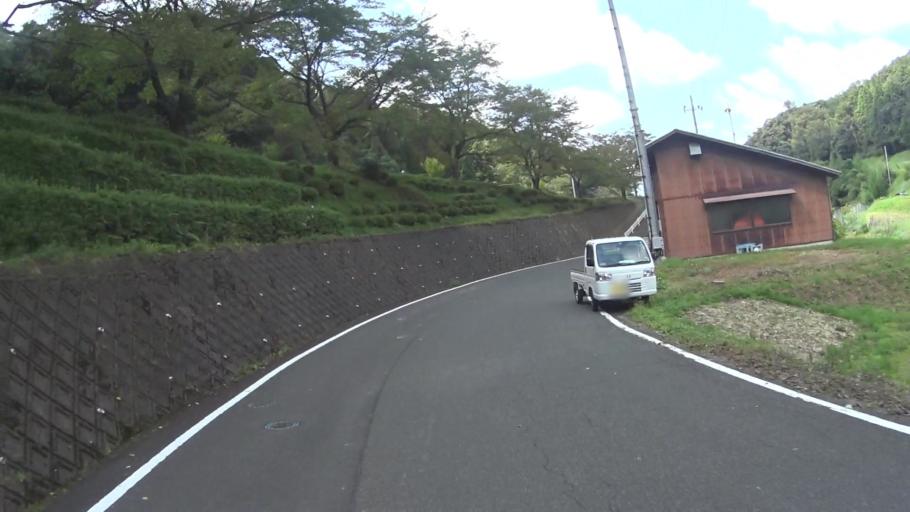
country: JP
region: Kyoto
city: Miyazu
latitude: 35.7439
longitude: 135.1811
